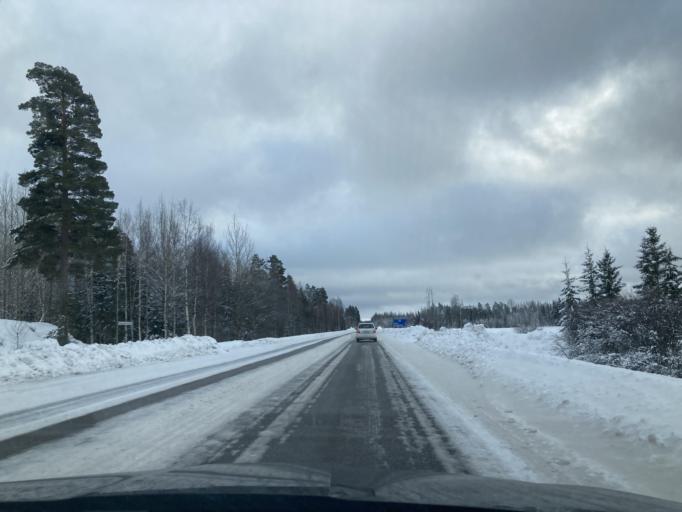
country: FI
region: Central Finland
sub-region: Jaemsae
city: Kuhmoinen
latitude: 61.6653
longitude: 25.2745
